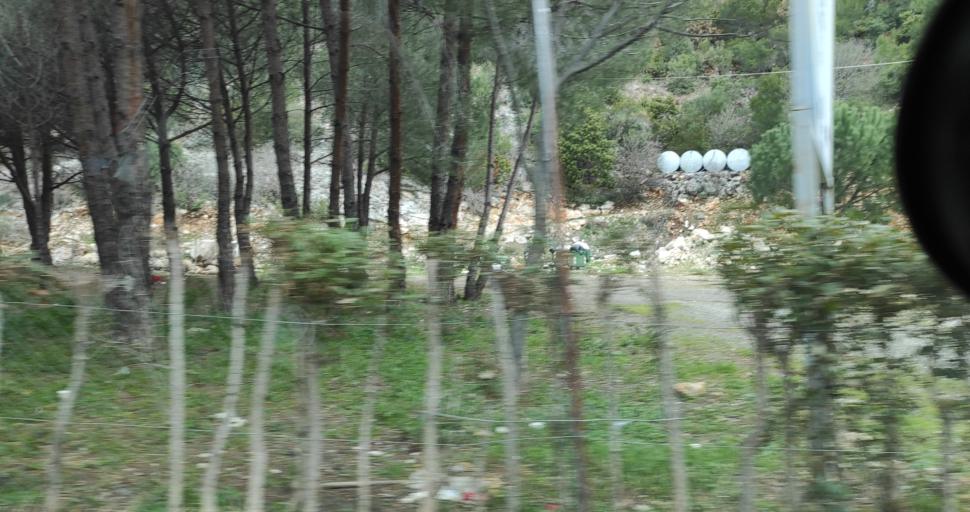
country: AL
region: Lezhe
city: Shengjin
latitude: 41.8248
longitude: 19.5588
